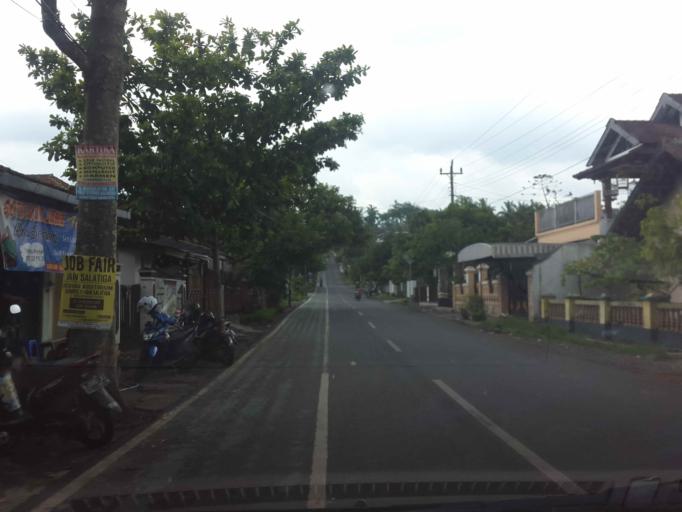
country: ID
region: Central Java
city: Salatiga
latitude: -7.3394
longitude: 110.4865
